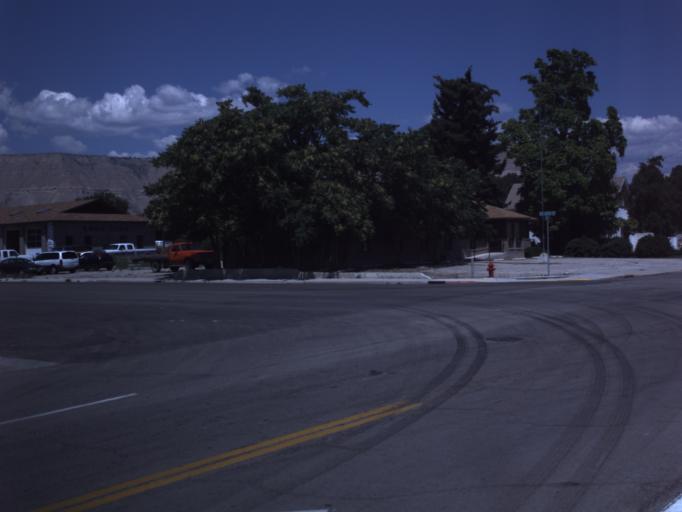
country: US
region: Utah
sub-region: Emery County
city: Ferron
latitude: 39.0881
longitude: -111.1320
